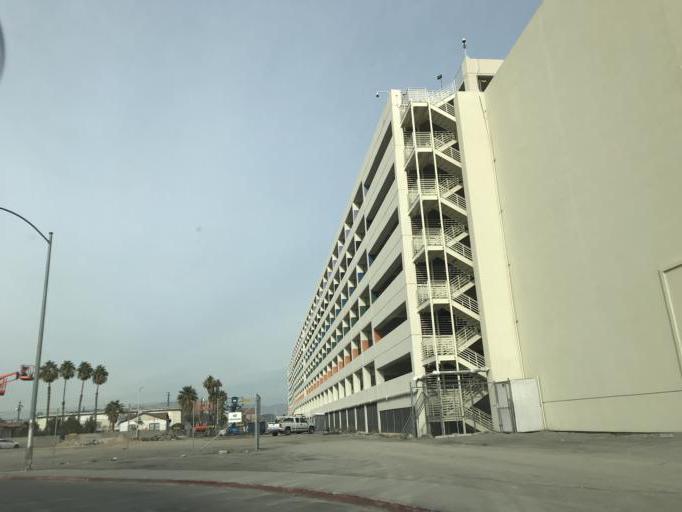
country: US
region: Nevada
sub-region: Clark County
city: Las Vegas
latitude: 36.1467
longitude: -115.1582
